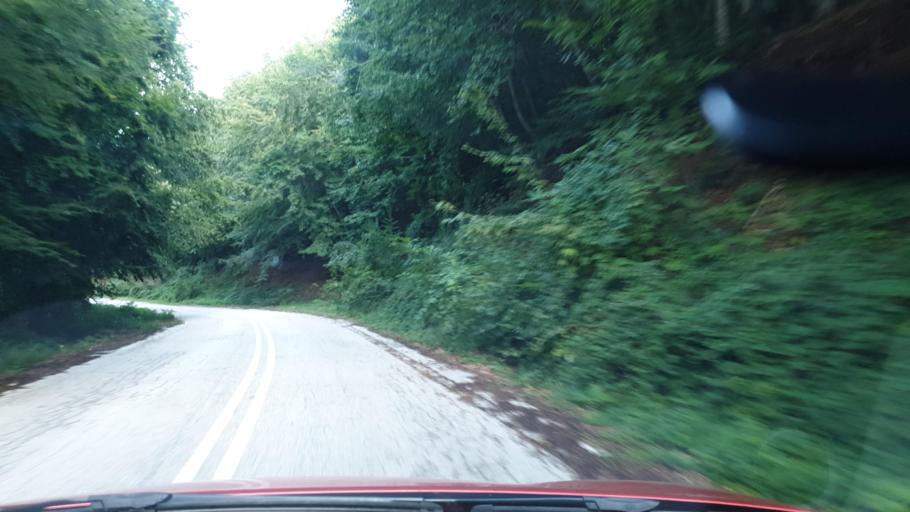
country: GR
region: Central Macedonia
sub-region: Nomos Chalkidikis
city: Galatista
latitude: 40.5088
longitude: 23.2556
